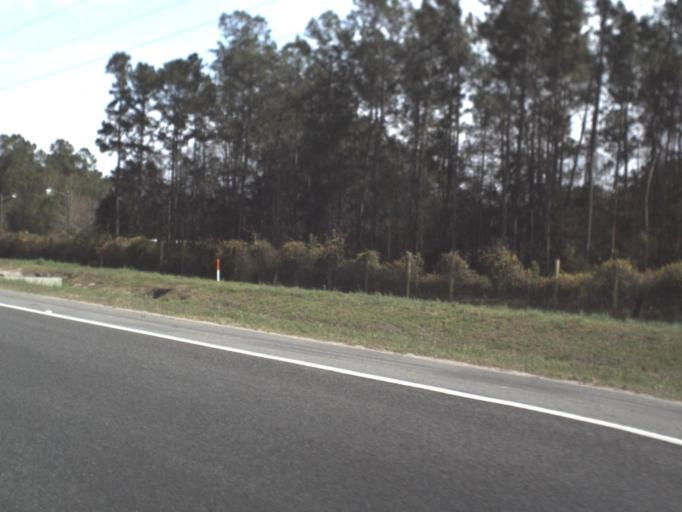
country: US
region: Florida
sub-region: Leon County
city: Tallahassee
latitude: 30.4783
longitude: -84.3562
